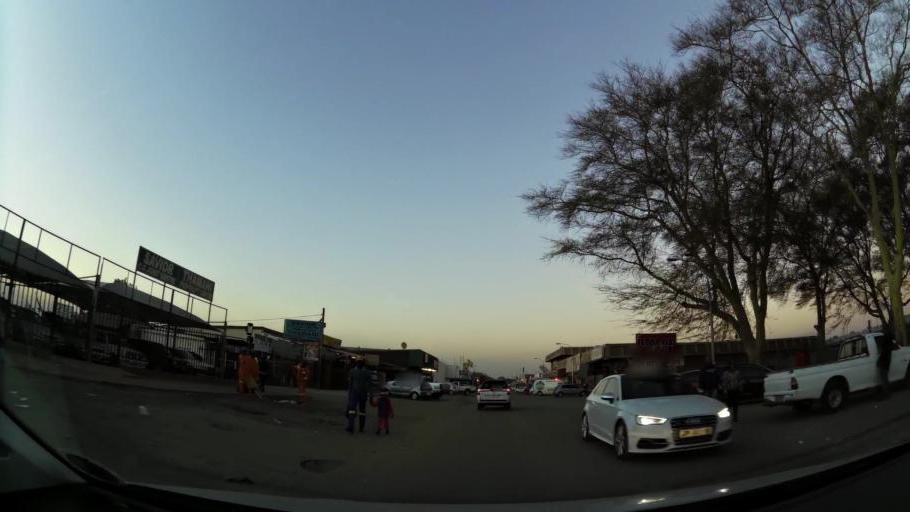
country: ZA
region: North-West
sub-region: Bojanala Platinum District Municipality
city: Rustenburg
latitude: -25.6649
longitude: 27.2373
